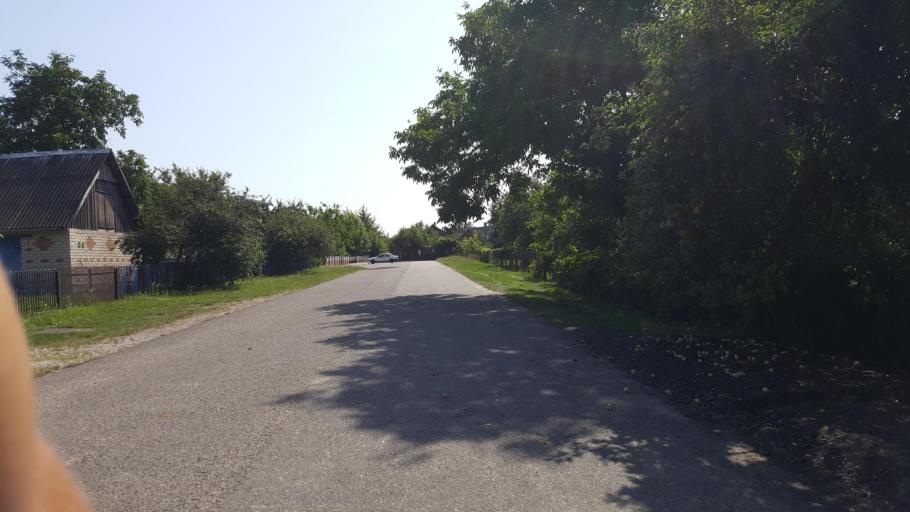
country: BY
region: Brest
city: Zhabinka
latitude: 52.1979
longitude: 24.0207
